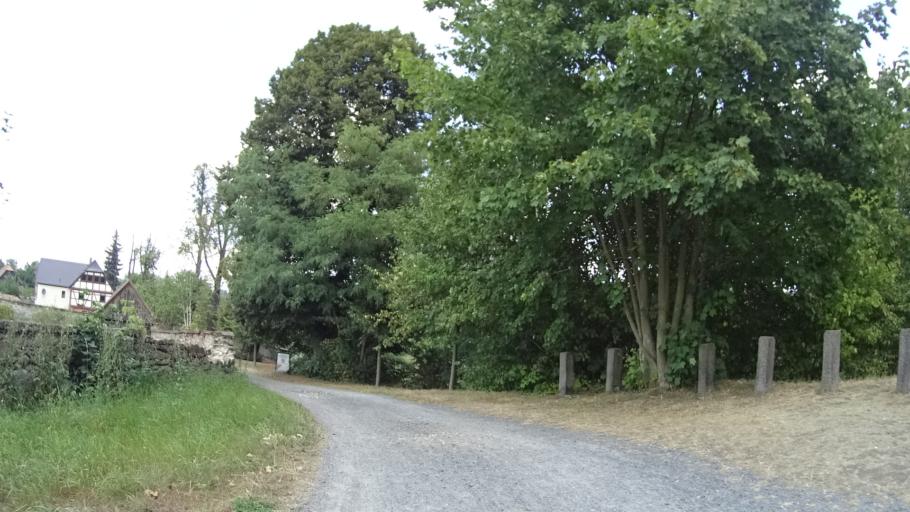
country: DE
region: Saxony
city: Ostritz
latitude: 50.9985
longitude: 14.9288
